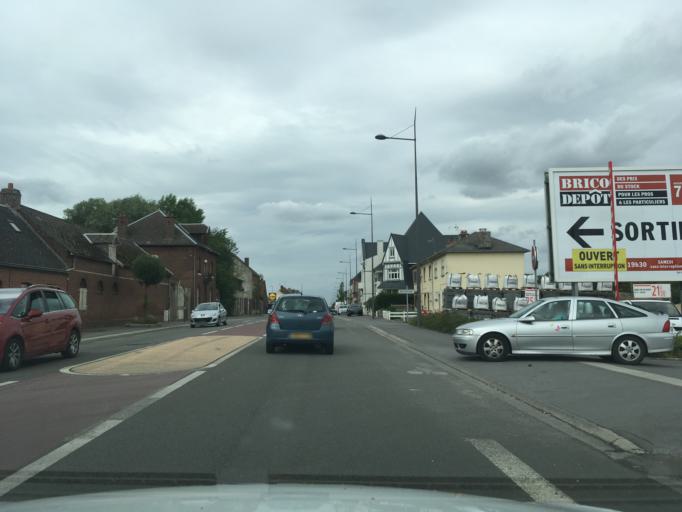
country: FR
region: Nord-Pas-de-Calais
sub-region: Departement du Nord
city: Cambrai
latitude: 50.1546
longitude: 3.2222
